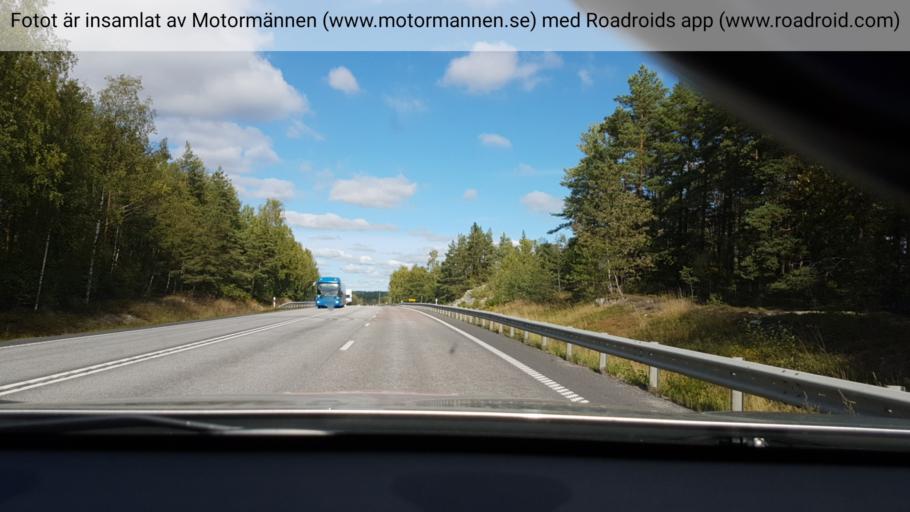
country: SE
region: Stockholm
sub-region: Osterakers Kommun
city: Akersberga
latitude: 59.4392
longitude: 18.2215
